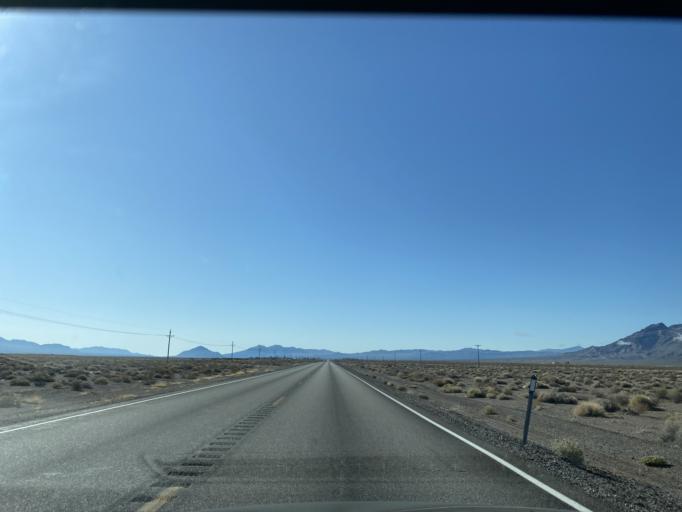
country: US
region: Nevada
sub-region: Nye County
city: Pahrump
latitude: 36.4416
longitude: -116.4220
